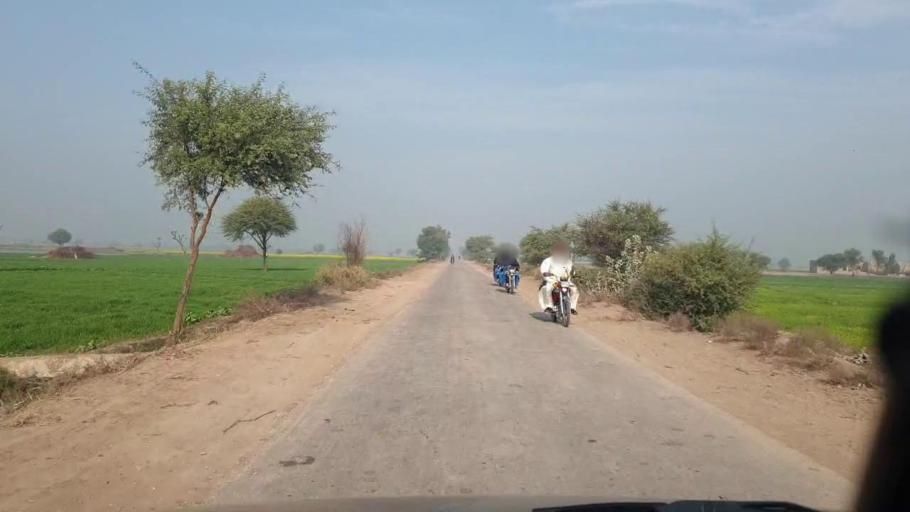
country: PK
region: Sindh
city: Shahdadpur
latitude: 25.9708
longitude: 68.5789
